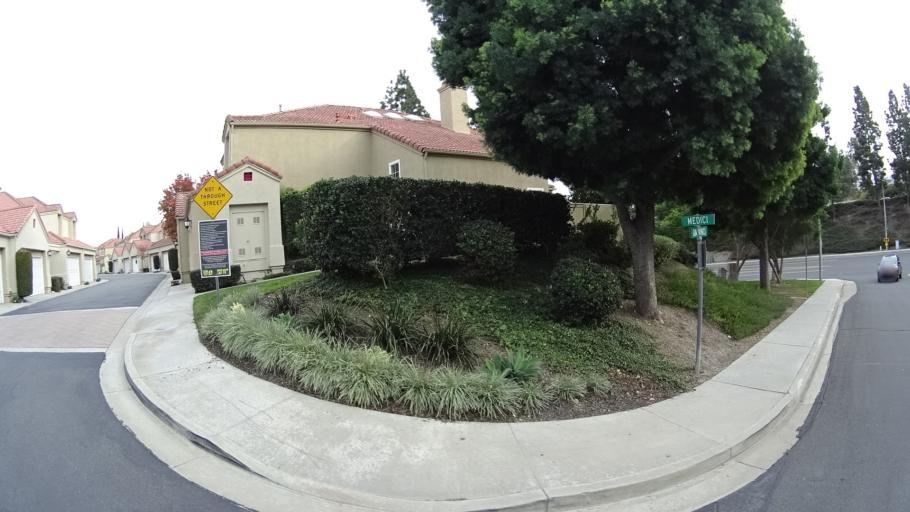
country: US
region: California
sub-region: Orange County
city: Laguna Woods
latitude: 33.5961
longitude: -117.7184
